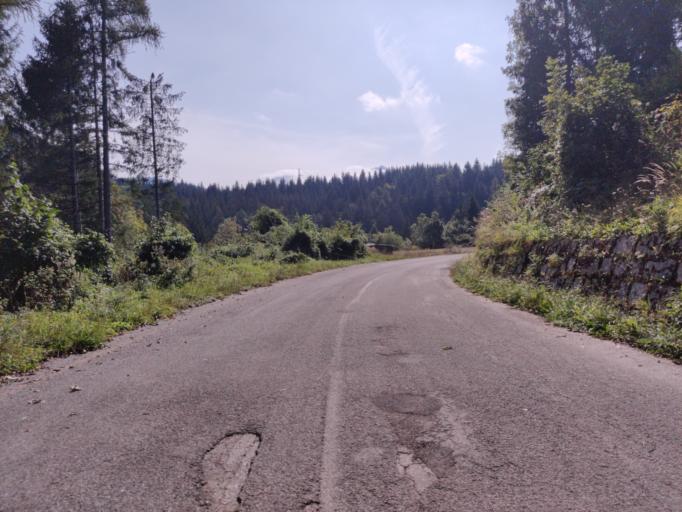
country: IT
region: Friuli Venezia Giulia
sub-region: Provincia di Udine
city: Tarvisio
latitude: 46.5168
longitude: 13.6145
